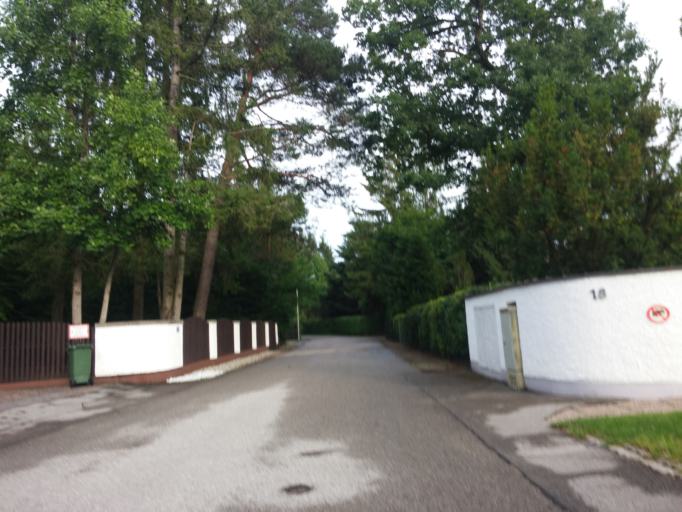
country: DE
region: Bavaria
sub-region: Upper Bavaria
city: Vaterstetten
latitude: 48.0895
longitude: 11.7912
